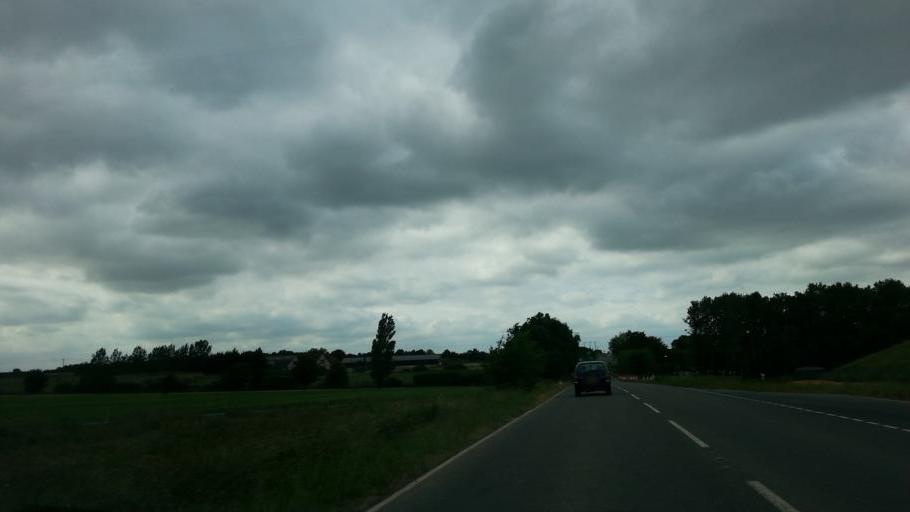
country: GB
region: England
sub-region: Cambridgeshire
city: Godmanchester
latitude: 52.2941
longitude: -0.1509
